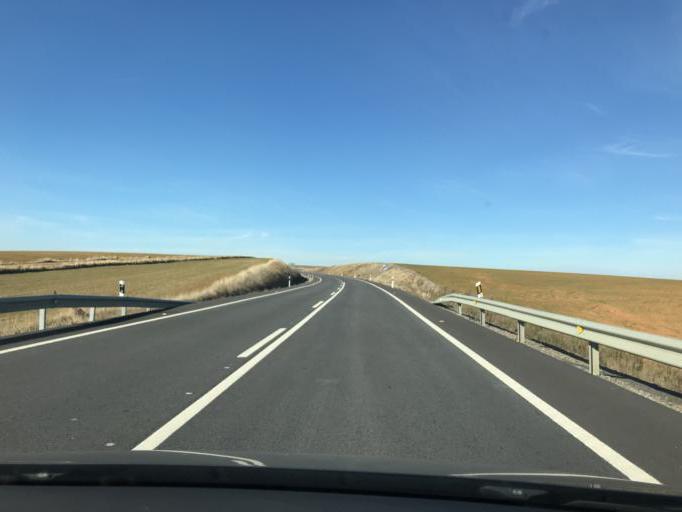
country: ES
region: Extremadura
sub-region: Provincia de Badajoz
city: Granja de Torrehermosa
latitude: 38.2966
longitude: -5.5505
